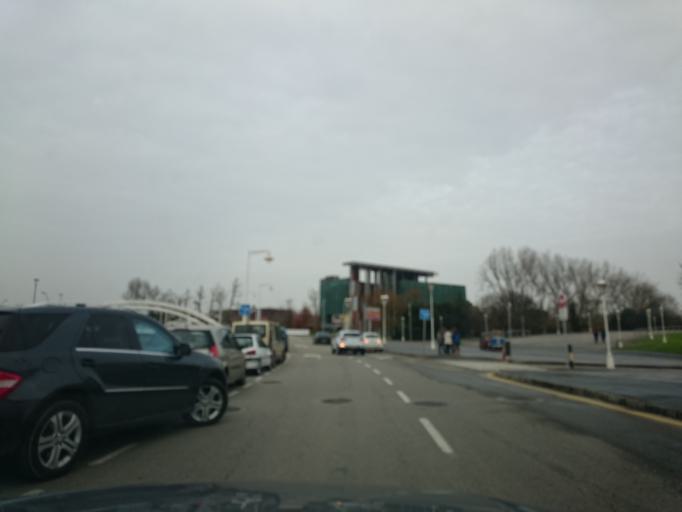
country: ES
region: Asturias
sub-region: Province of Asturias
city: Gijon
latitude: 43.5357
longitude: -5.6343
